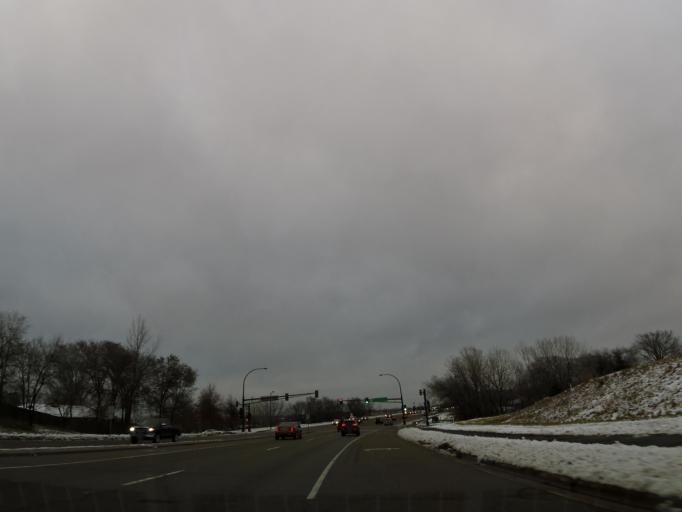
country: US
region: Minnesota
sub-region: Dakota County
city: Apple Valley
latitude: 44.7165
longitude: -93.2544
